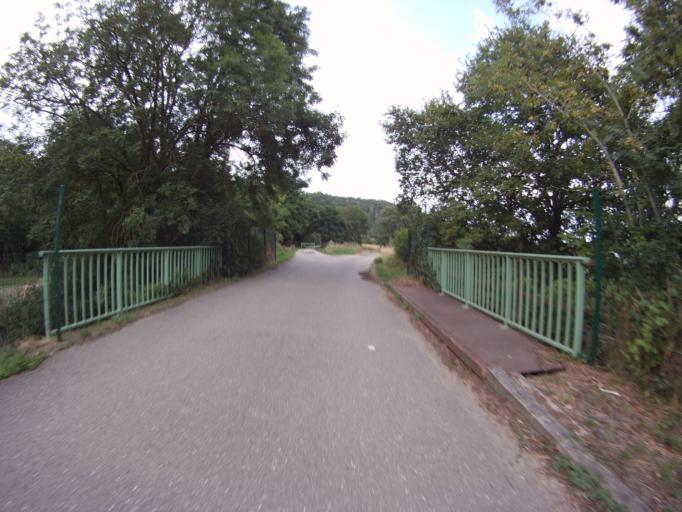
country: FR
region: Lorraine
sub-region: Departement de la Moselle
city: Courcelles-Chaussy
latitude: 49.0894
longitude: 6.3598
